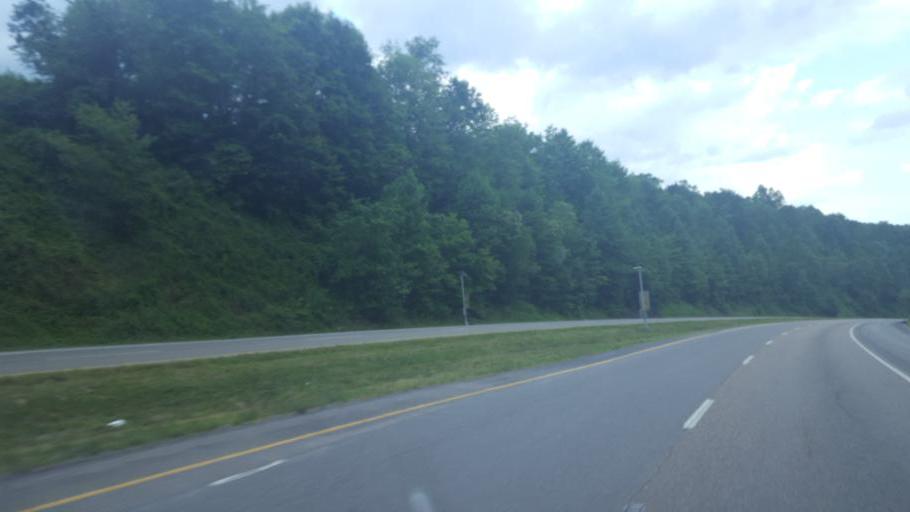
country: US
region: Virginia
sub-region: Wise County
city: Pound
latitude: 37.1085
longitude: -82.5999
